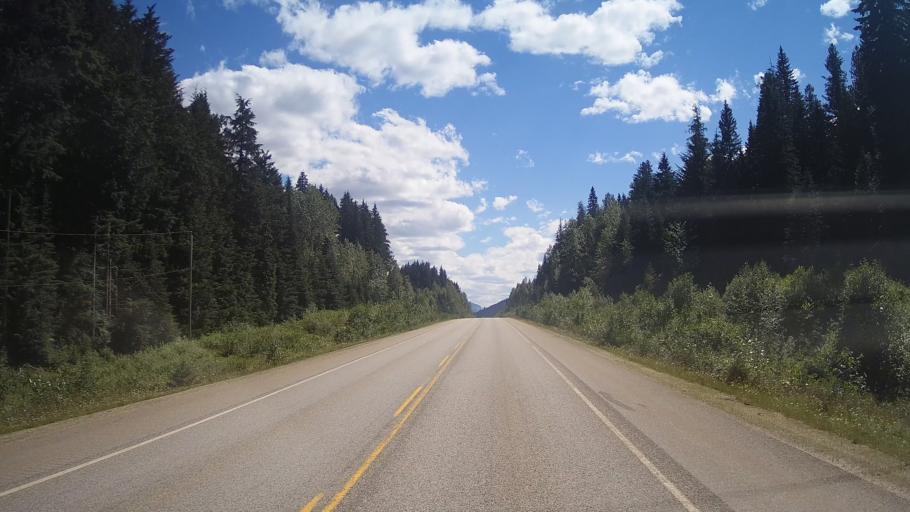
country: CA
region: Alberta
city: Jasper Park Lodge
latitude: 52.5559
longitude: -119.1111
